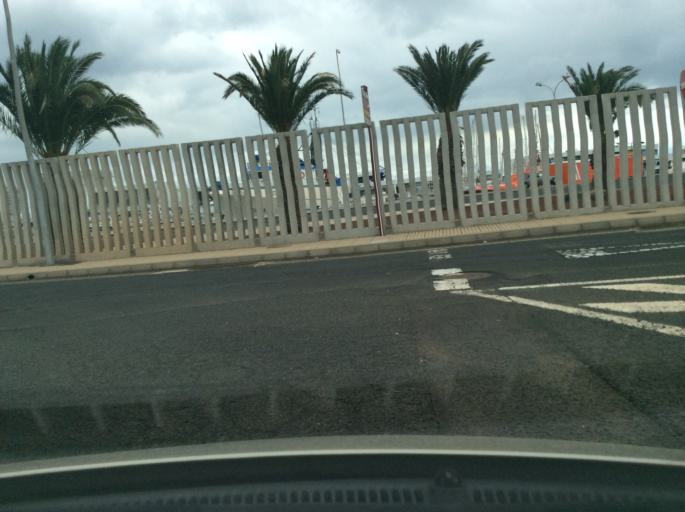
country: ES
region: Canary Islands
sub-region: Provincia de Las Palmas
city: Arrecife
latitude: 28.9652
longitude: -13.5403
